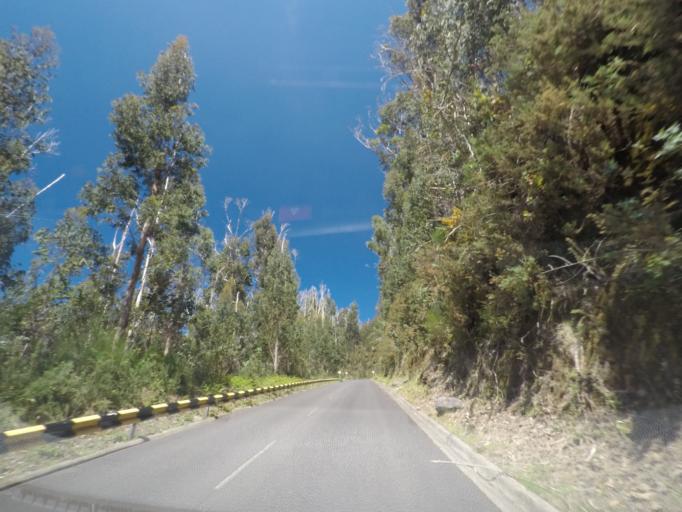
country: PT
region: Madeira
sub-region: Calheta
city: Arco da Calheta
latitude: 32.7403
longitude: -17.1282
